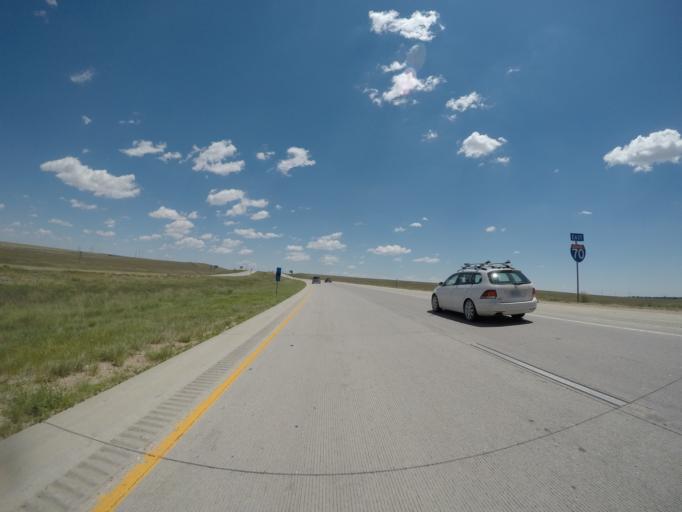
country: US
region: Colorado
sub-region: Lincoln County
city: Limon
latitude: 39.2608
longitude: -103.6584
